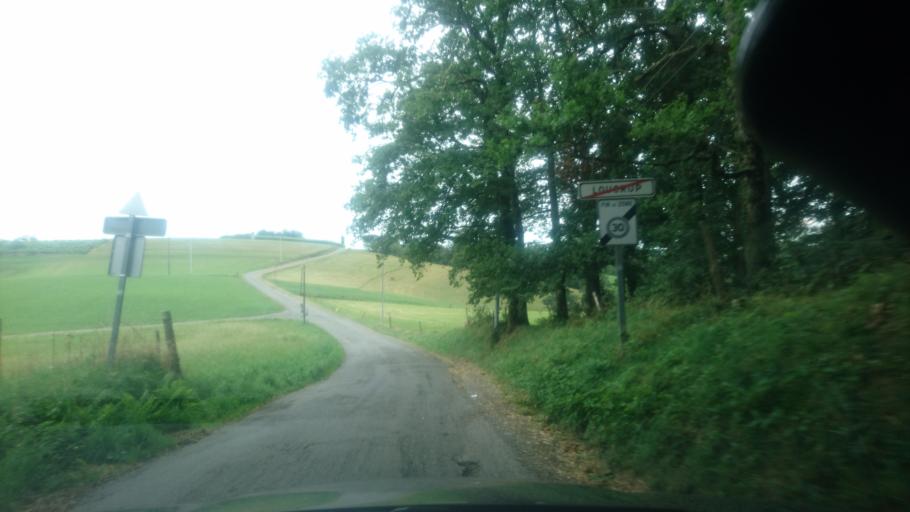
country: FR
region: Midi-Pyrenees
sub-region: Departement des Hautes-Pyrenees
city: Horgues
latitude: 43.1251
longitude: 0.0608
